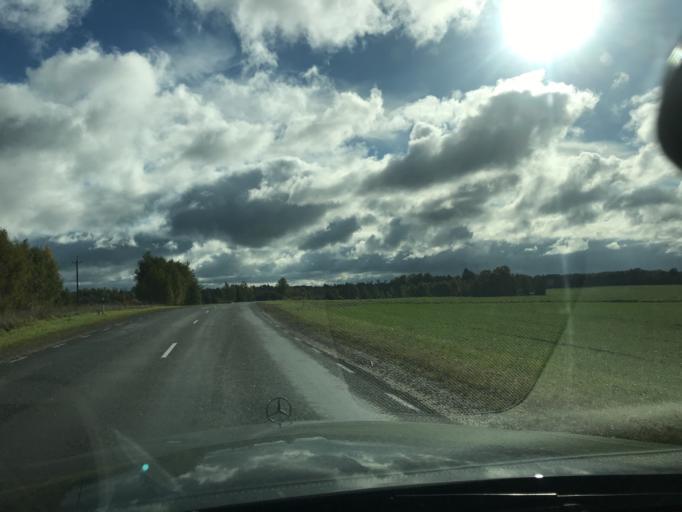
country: EE
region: Tartu
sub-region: Elva linn
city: Elva
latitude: 58.0070
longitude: 26.2593
